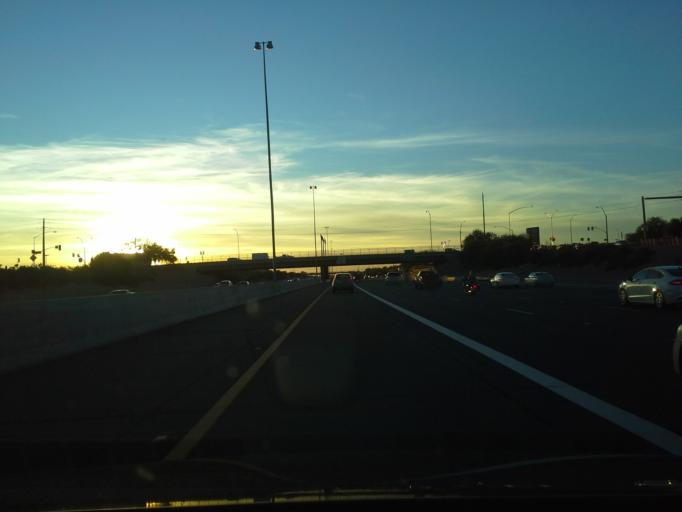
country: US
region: Arizona
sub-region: Maricopa County
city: Gilbert
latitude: 33.3866
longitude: -111.6826
